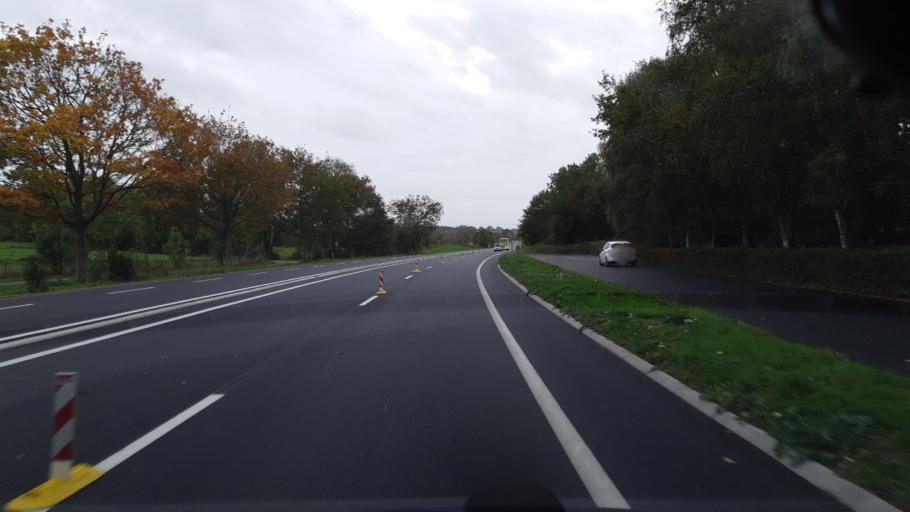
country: FR
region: Lower Normandy
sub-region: Departement de la Manche
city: Brehal
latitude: 48.8945
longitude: -1.5043
